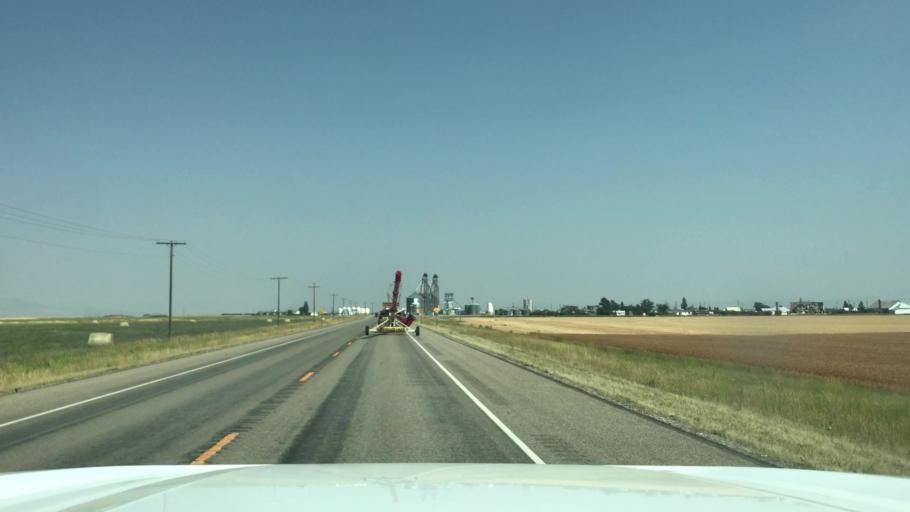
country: US
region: Montana
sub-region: Judith Basin County
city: Stanford
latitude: 47.0552
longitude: -109.9210
